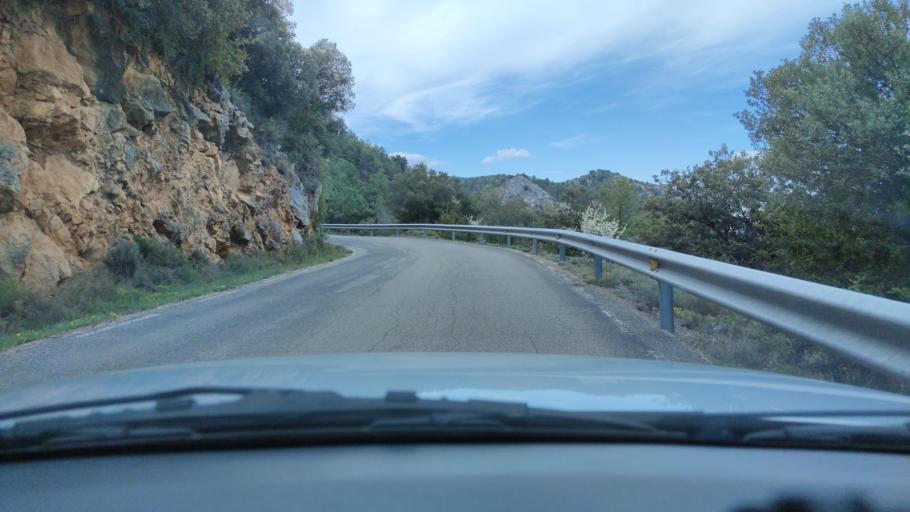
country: ES
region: Catalonia
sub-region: Provincia de Lleida
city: Coll de Nargo
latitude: 42.2471
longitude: 1.3682
